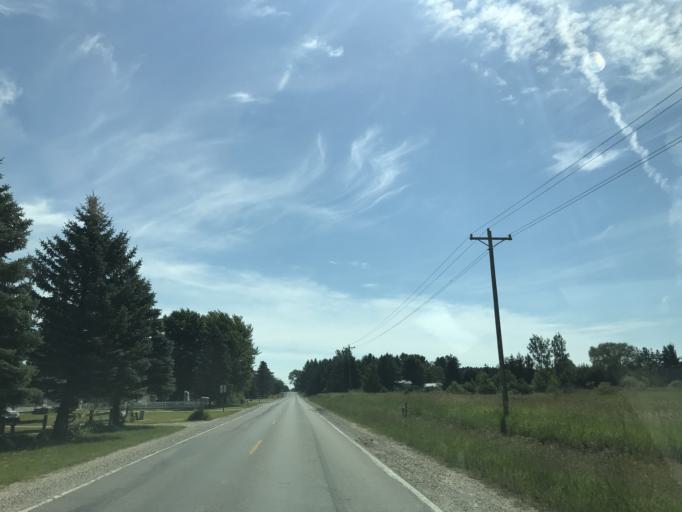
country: US
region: Michigan
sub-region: Grand Traverse County
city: Traverse City
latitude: 44.6577
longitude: -85.6893
